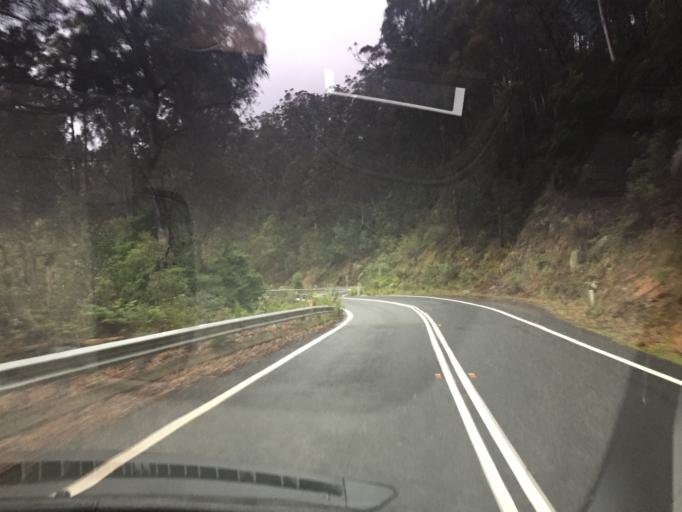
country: AU
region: New South Wales
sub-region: Bega Valley
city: Bega
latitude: -36.6087
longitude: 149.4693
